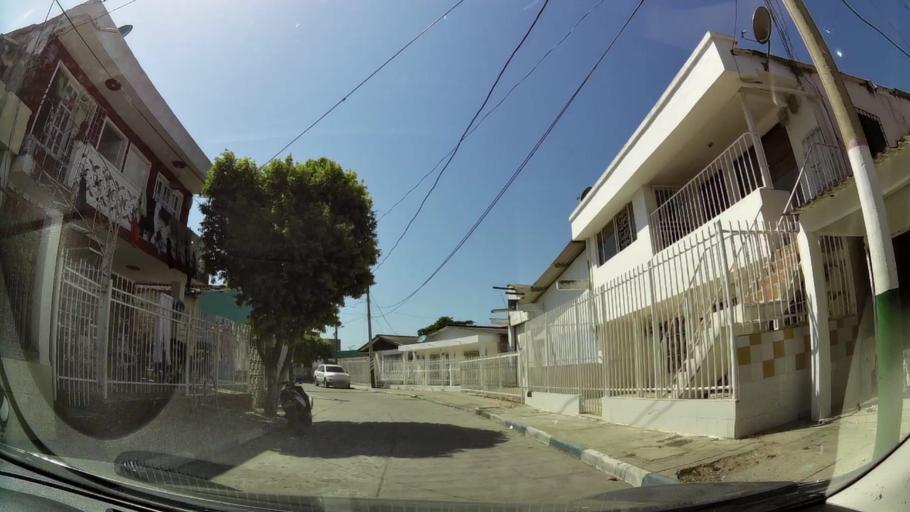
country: CO
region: Bolivar
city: Cartagena
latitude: 10.4363
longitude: -75.5254
